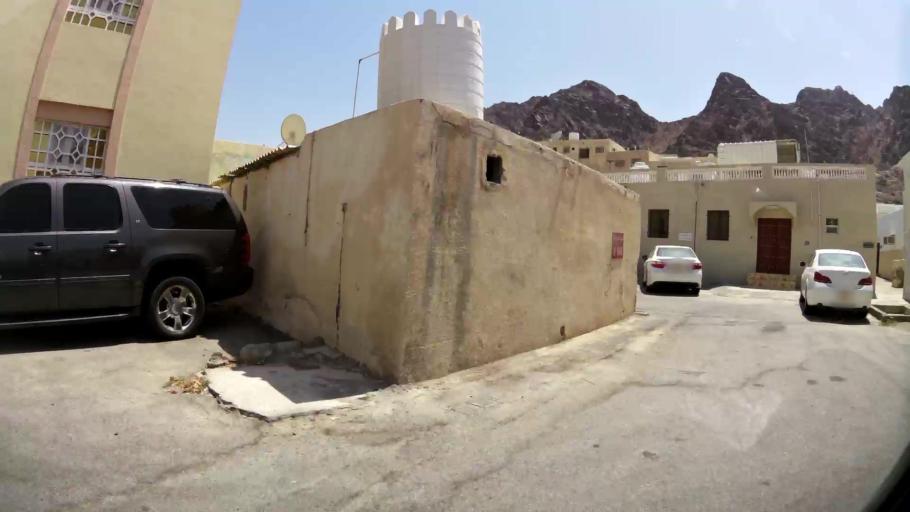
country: OM
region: Muhafazat Masqat
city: Muscat
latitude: 23.6051
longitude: 58.5971
